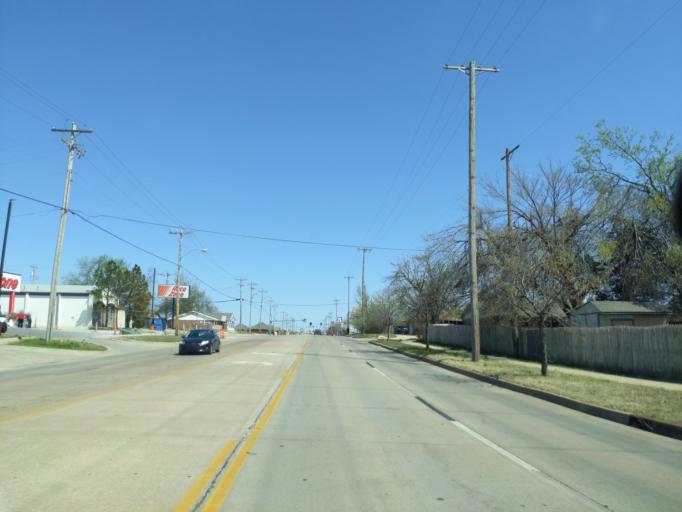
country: US
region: Oklahoma
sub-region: Cleveland County
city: Moore
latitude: 35.3488
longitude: -97.5015
